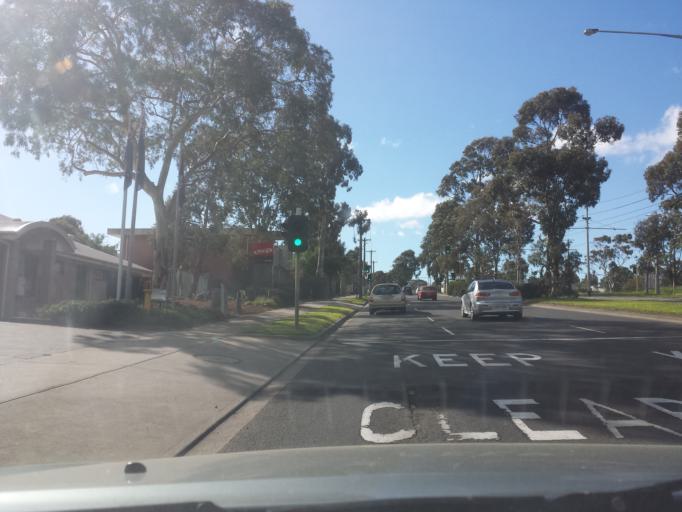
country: AU
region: Victoria
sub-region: Darebin
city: Kingsbury
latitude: -37.7109
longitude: 145.0482
